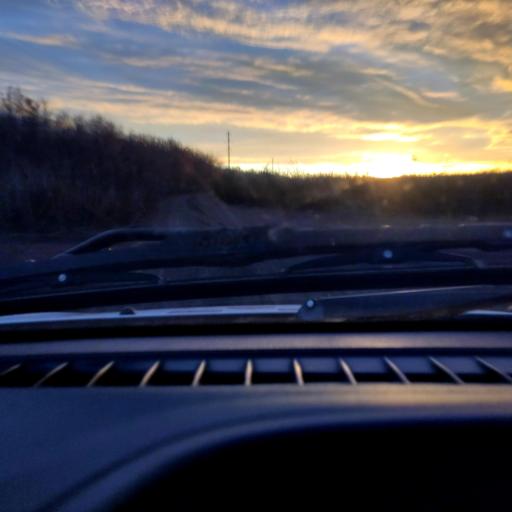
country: RU
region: Samara
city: Tol'yatti
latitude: 53.5968
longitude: 49.4689
